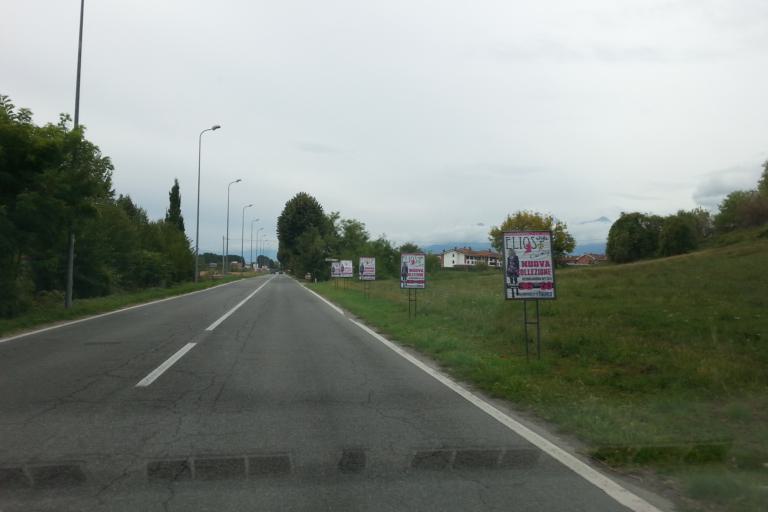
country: IT
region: Piedmont
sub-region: Provincia di Torino
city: Riva
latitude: 44.8980
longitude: 7.3569
